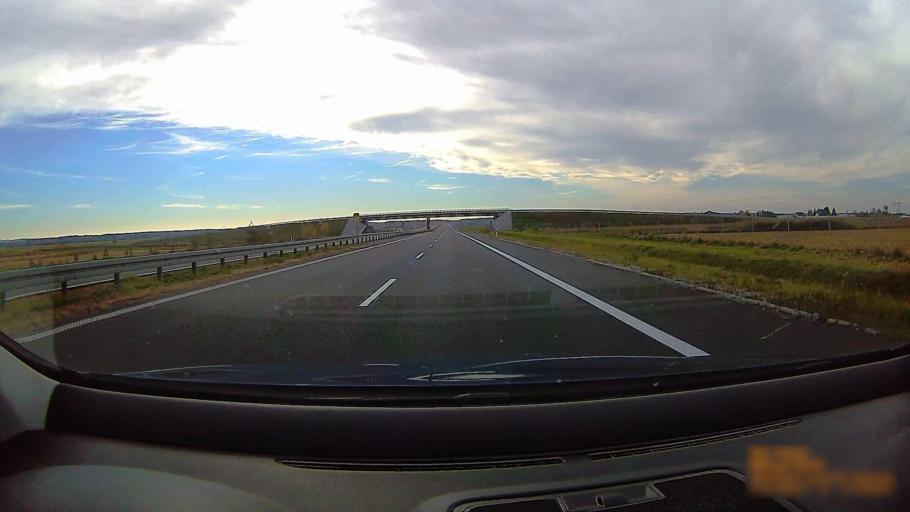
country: PL
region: Greater Poland Voivodeship
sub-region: Powiat ostrowski
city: Przygodzice
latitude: 51.5927
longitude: 17.8502
